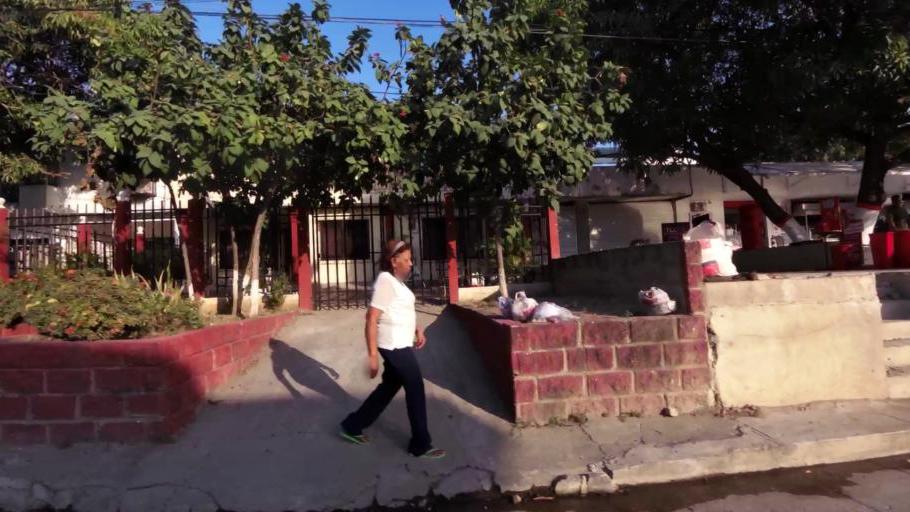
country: CO
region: Bolivar
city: Cartagena
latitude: 10.3827
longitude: -75.4801
